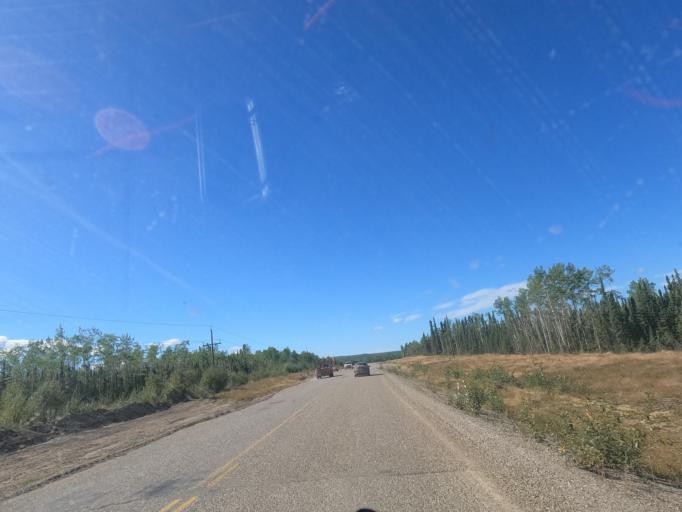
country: CA
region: Yukon
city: Dawson City
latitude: 63.8729
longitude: -138.1284
